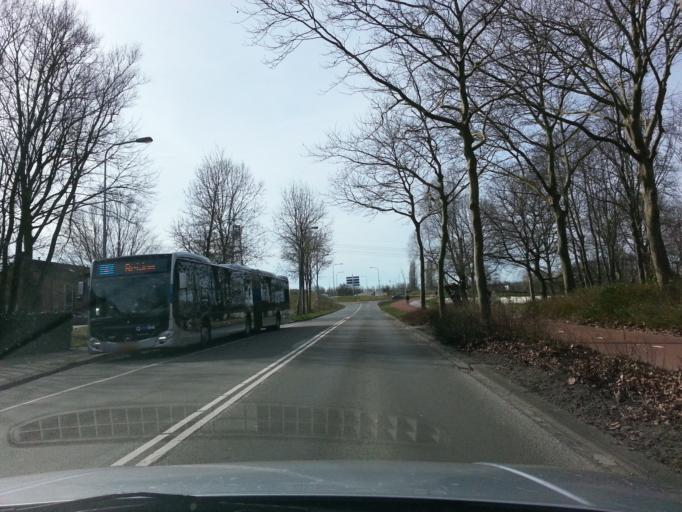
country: NL
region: Groningen
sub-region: Gemeente Groningen
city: Oosterpark
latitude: 53.2429
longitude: 6.5886
